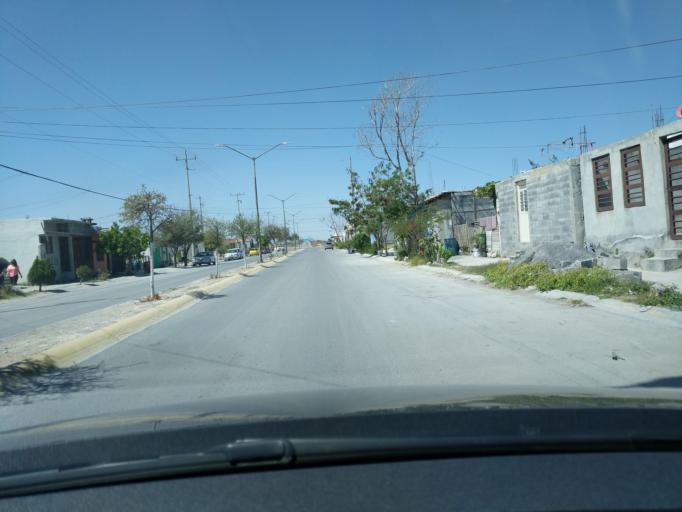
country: MX
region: Nuevo Leon
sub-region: Pesqueria
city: Colinas del Aeropuerto
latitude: 25.8235
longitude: -100.1227
